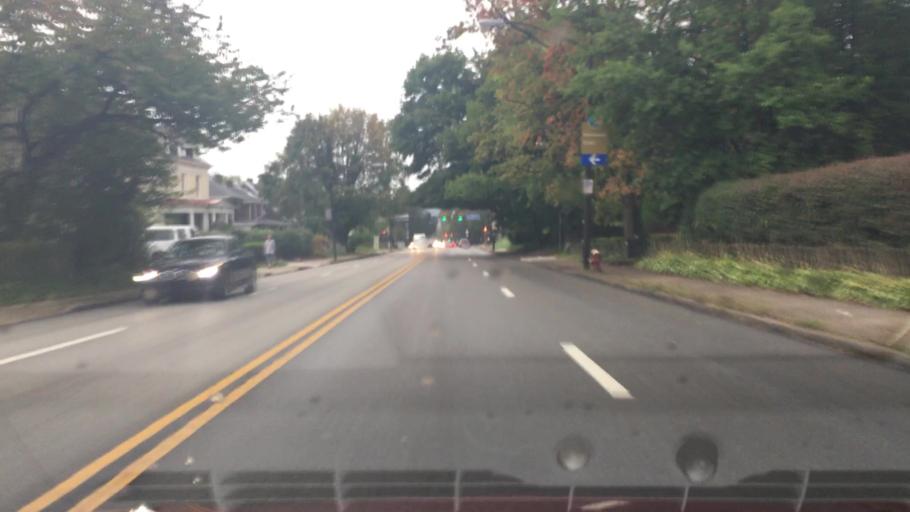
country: US
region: Pennsylvania
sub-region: Allegheny County
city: Wilkinsburg
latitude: 40.4497
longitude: -79.9031
